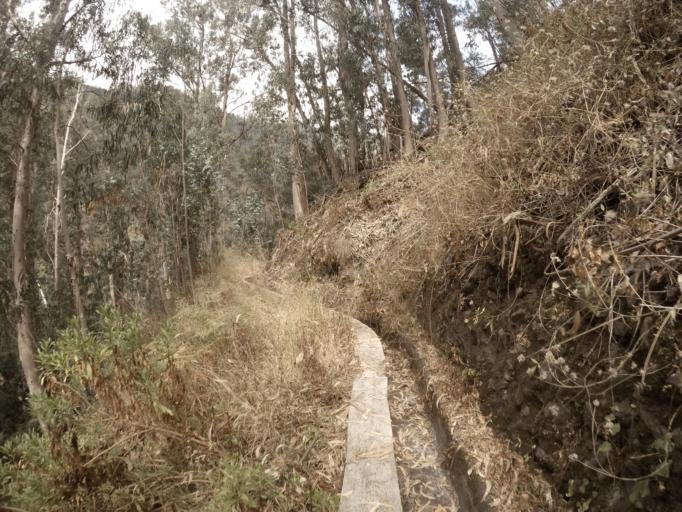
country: PT
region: Madeira
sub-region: Camara de Lobos
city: Curral das Freiras
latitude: 32.6844
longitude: -16.9622
